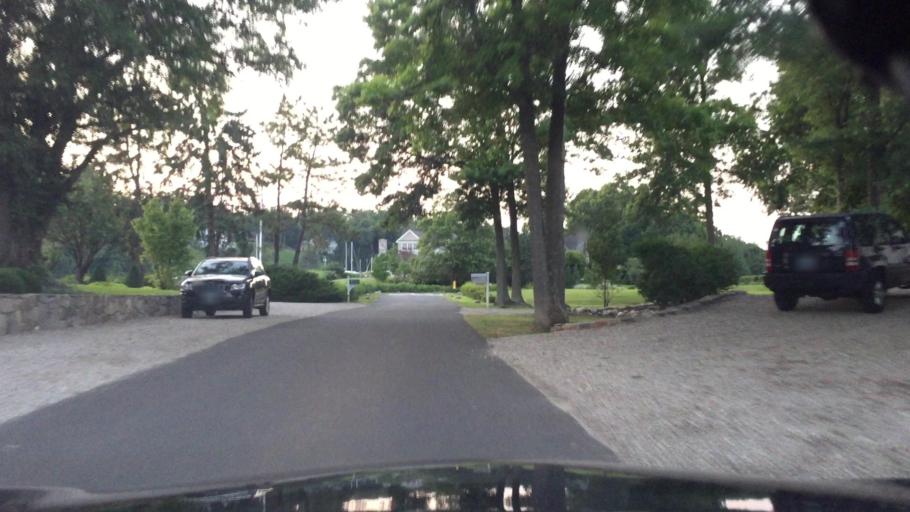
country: US
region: Connecticut
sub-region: Fairfield County
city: Darien
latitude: 41.0666
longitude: -73.4300
